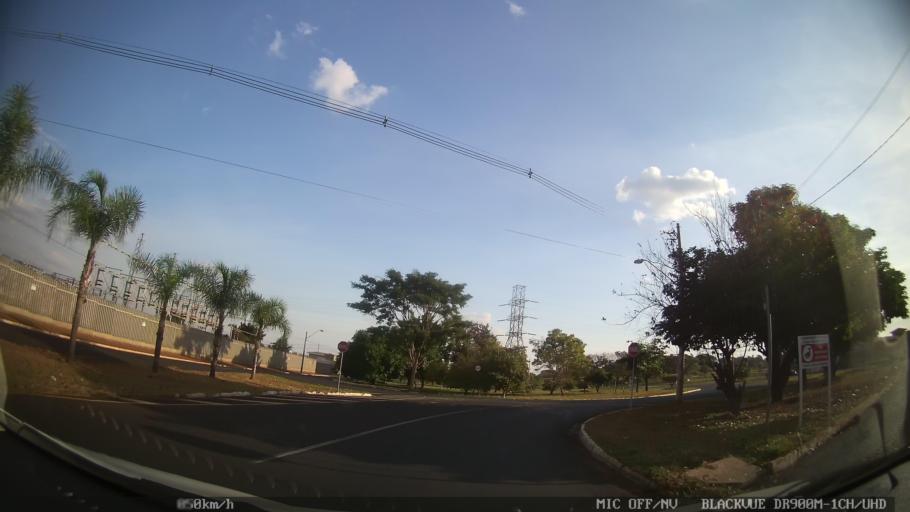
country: BR
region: Sao Paulo
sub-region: Ribeirao Preto
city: Ribeirao Preto
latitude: -21.1600
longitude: -47.8411
